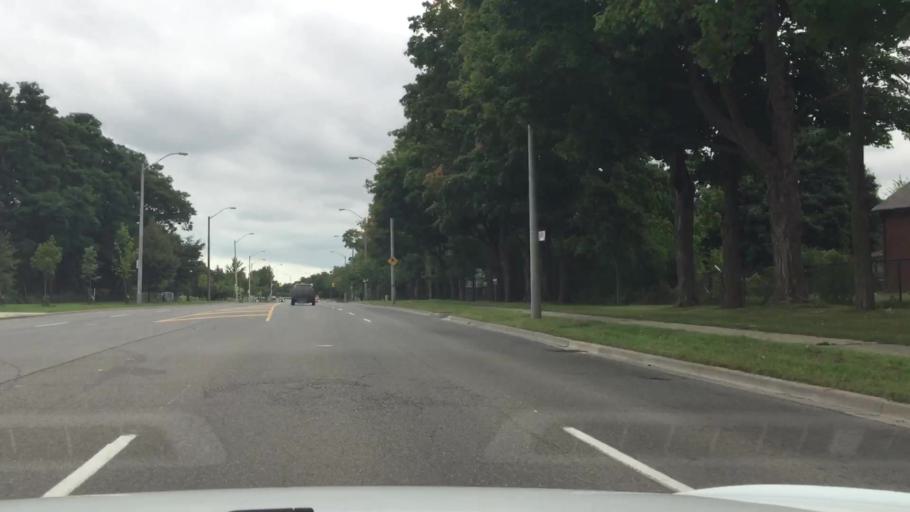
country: CA
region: Ontario
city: Scarborough
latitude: 43.8146
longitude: -79.2268
